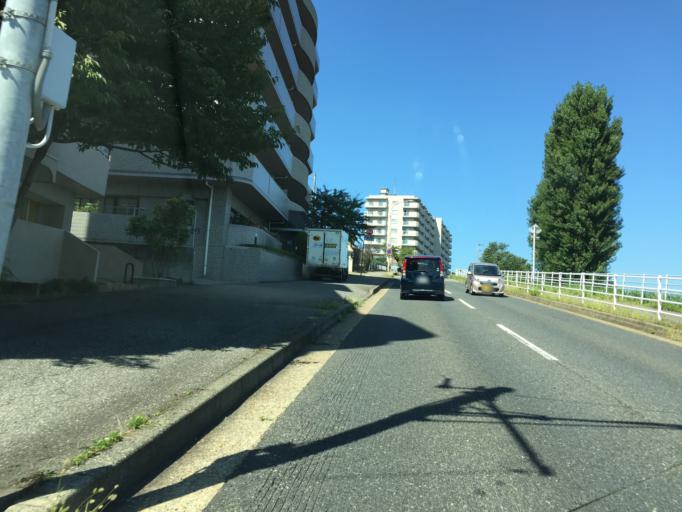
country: JP
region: Niigata
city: Niigata-shi
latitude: 37.8997
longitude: 139.0073
